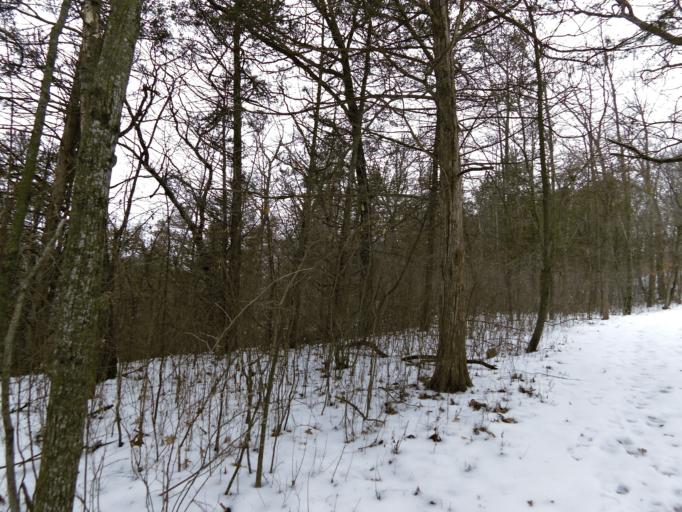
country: US
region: Wisconsin
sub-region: Pierce County
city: Prescott
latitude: 44.7994
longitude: -92.7913
